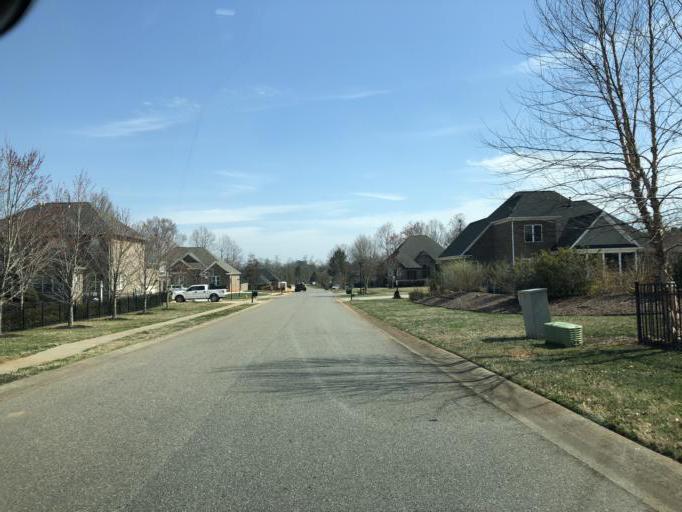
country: US
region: North Carolina
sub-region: Gaston County
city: Stanley
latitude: 35.3424
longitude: -81.0900
